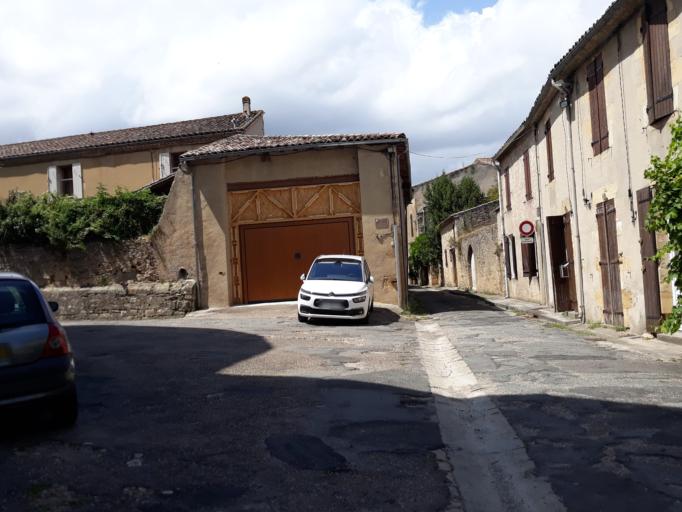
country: FR
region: Aquitaine
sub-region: Departement de la Gironde
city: Saint-Macaire
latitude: 44.5640
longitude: -0.2253
